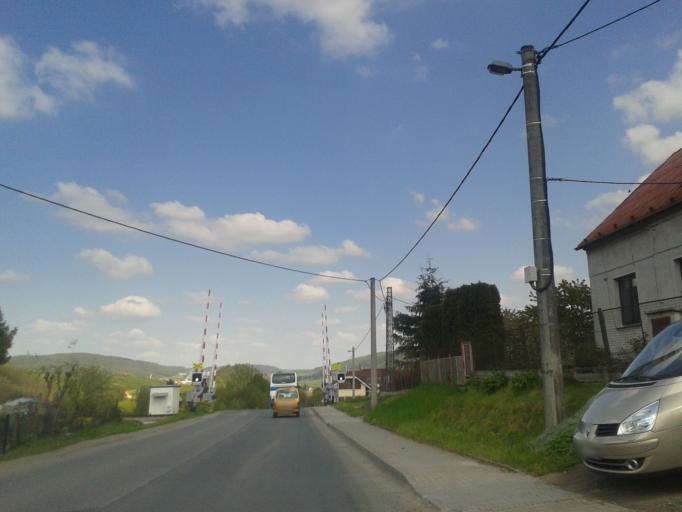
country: CZ
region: Central Bohemia
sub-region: Okres Beroun
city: Lodenice
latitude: 49.9863
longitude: 14.1341
